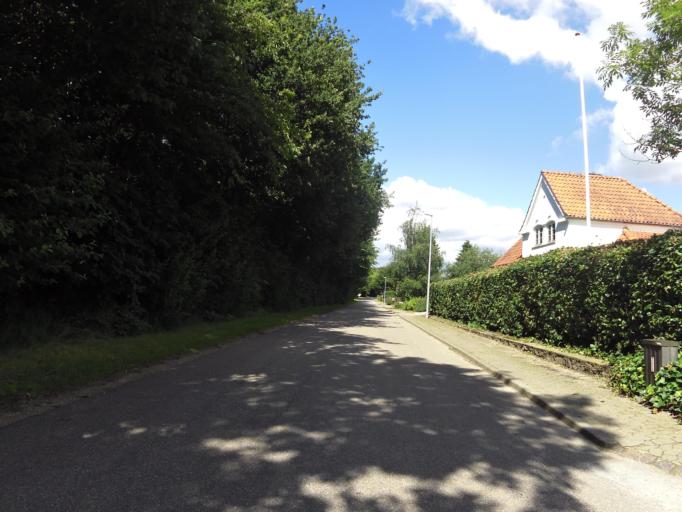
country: DK
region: South Denmark
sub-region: Haderslev Kommune
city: Gram
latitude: 55.3076
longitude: 9.1500
